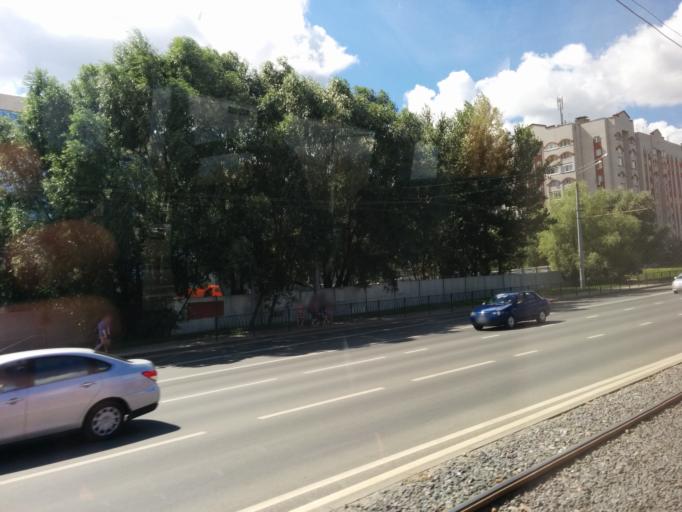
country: RU
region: Tatarstan
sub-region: Gorod Kazan'
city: Kazan
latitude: 55.8271
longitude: 49.1088
